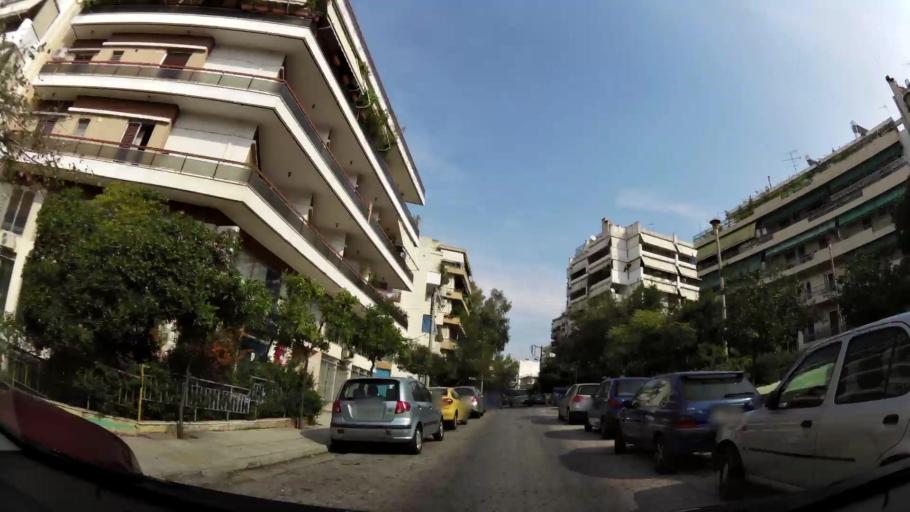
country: GR
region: Attica
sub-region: Nomarchia Athinas
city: Galatsi
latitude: 38.0130
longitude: 23.7561
